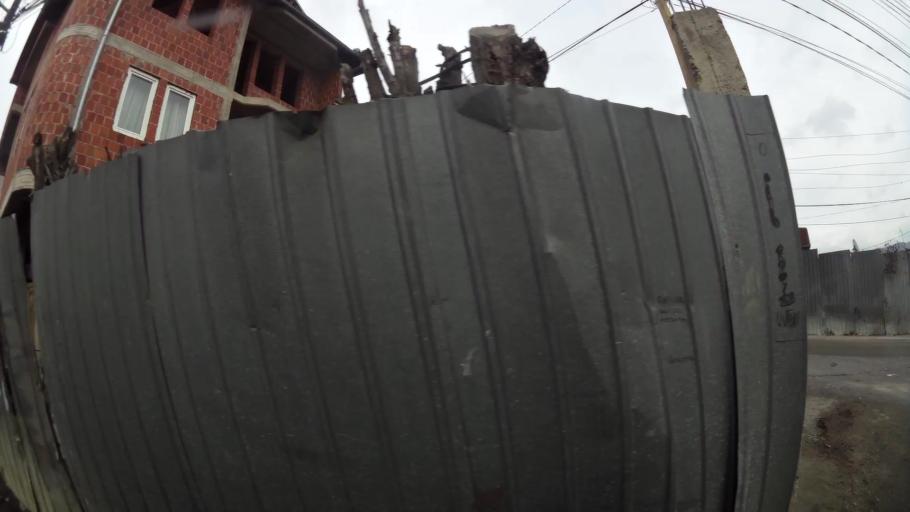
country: XK
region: Pristina
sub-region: Komuna e Prishtines
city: Pristina
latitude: 42.6790
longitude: 21.1704
